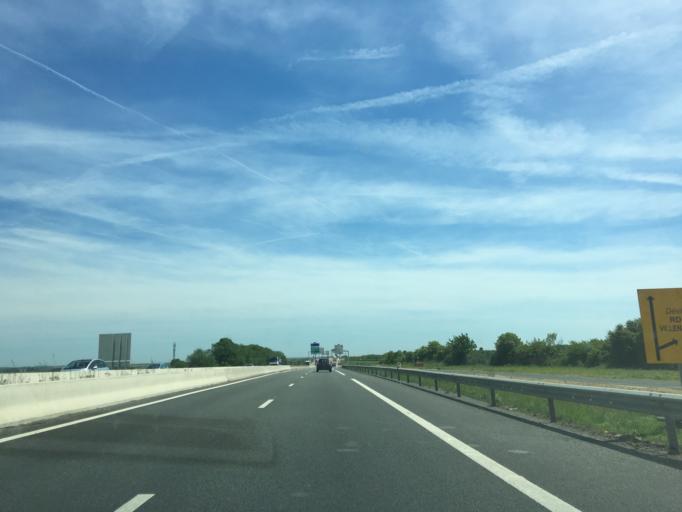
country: FR
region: Ile-de-France
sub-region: Departement de Seine-et-Marne
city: Mitry-Mory
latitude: 49.0059
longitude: 2.6226
